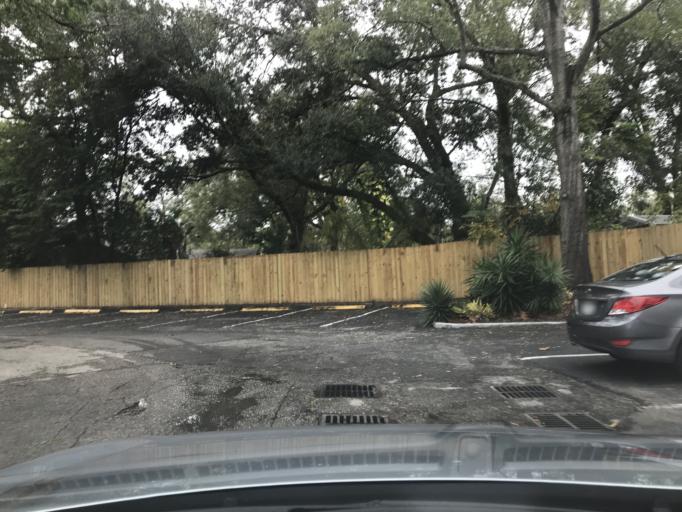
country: US
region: Florida
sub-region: Hillsborough County
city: Tampa
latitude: 27.9829
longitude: -82.4702
